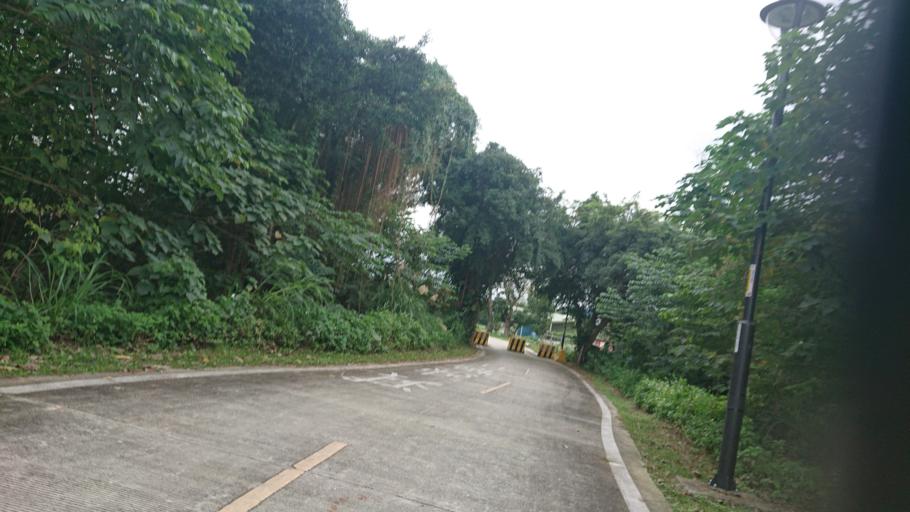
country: TW
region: Taiwan
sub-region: Taoyuan
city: Taoyuan
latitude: 24.9510
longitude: 121.3641
